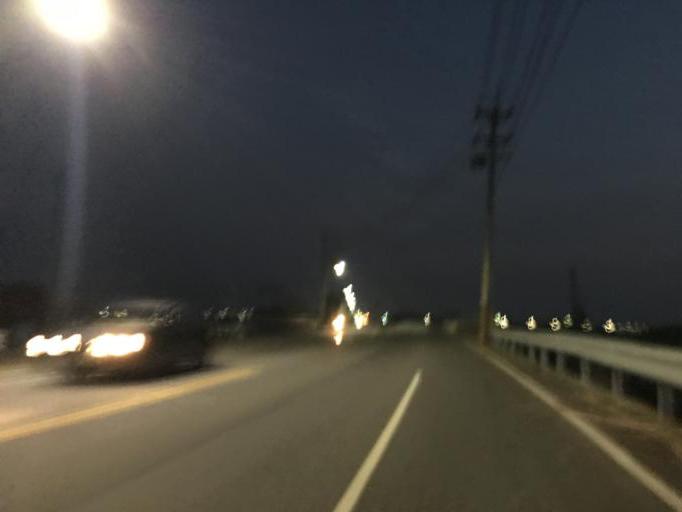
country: TW
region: Taiwan
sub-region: Chiayi
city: Taibao
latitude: 23.5229
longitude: 120.3207
